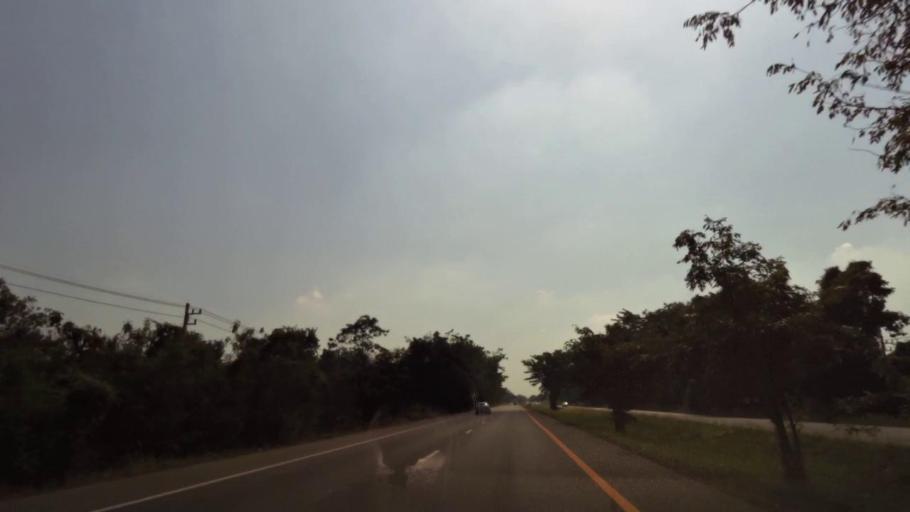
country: TH
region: Phichit
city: Bueng Na Rang
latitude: 16.2009
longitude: 100.1280
